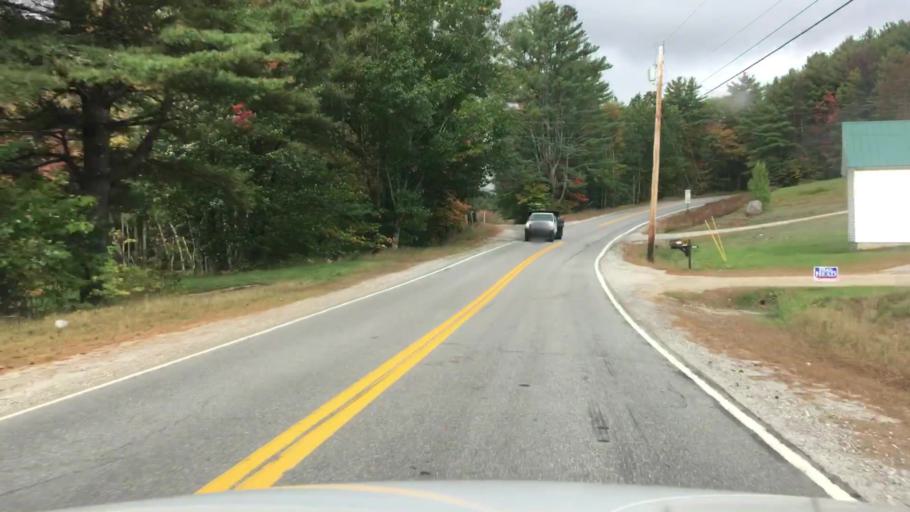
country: US
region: Maine
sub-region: Oxford County
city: Bethel
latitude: 44.3394
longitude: -70.7821
